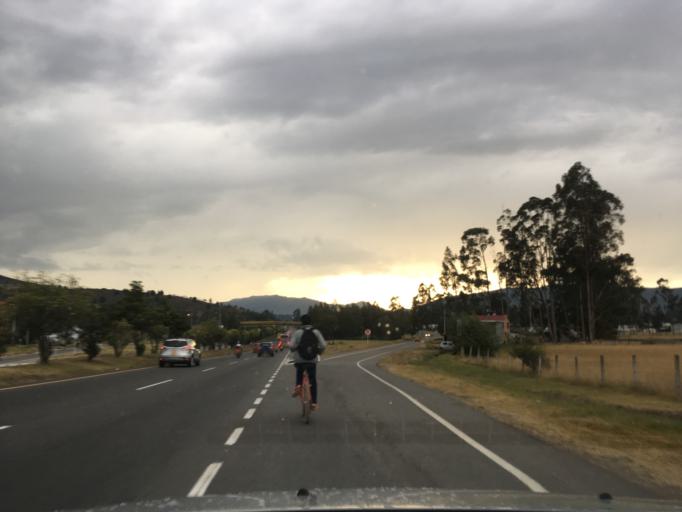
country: CO
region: Cundinamarca
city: Sesquile
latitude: 5.0563
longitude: -73.7945
